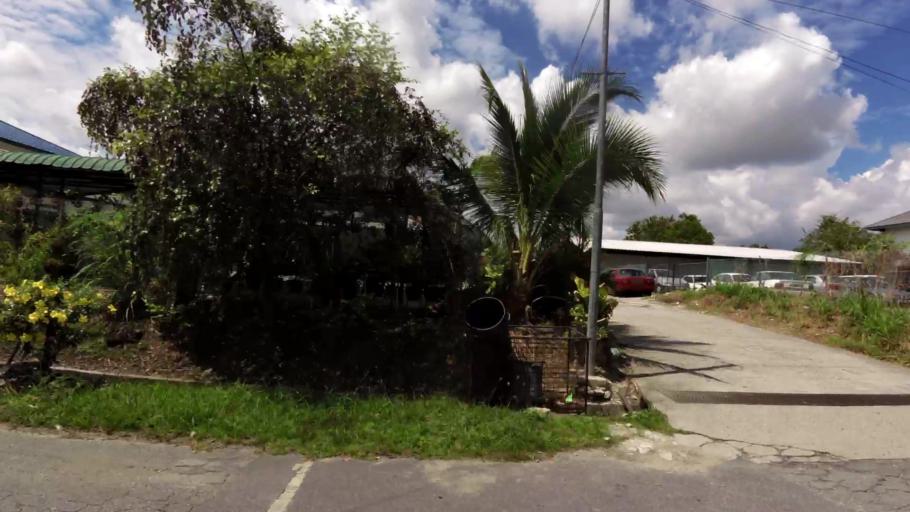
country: BN
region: Brunei and Muara
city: Bandar Seri Begawan
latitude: 4.9429
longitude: 114.9051
